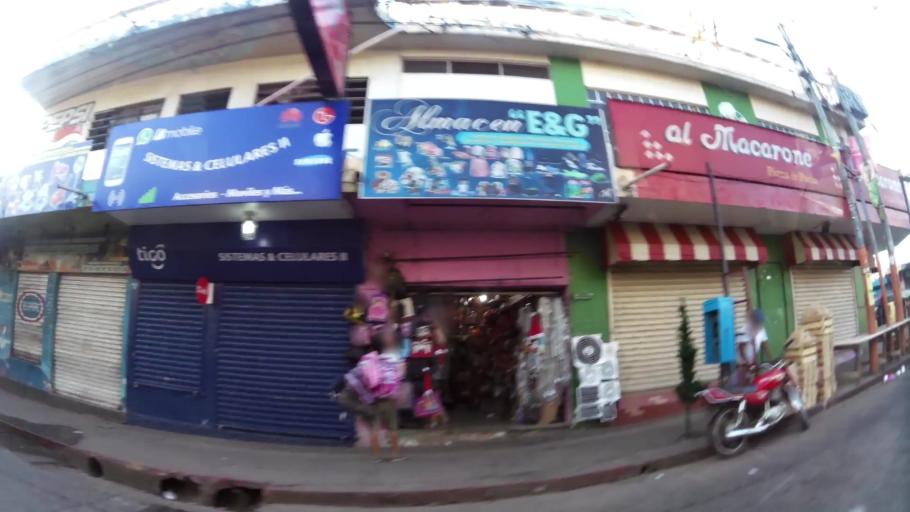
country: GT
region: Suchitepeque
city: Mazatenango
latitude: 14.5342
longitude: -91.5059
